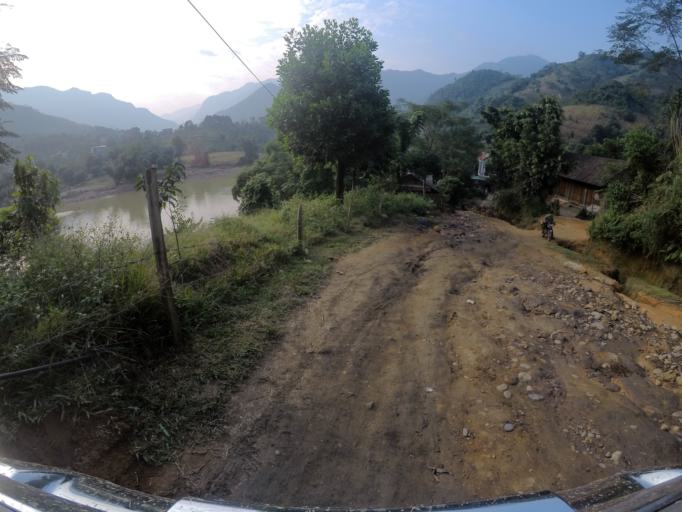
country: VN
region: Yen Bai
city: Son Thinh
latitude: 21.6818
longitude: 104.6155
